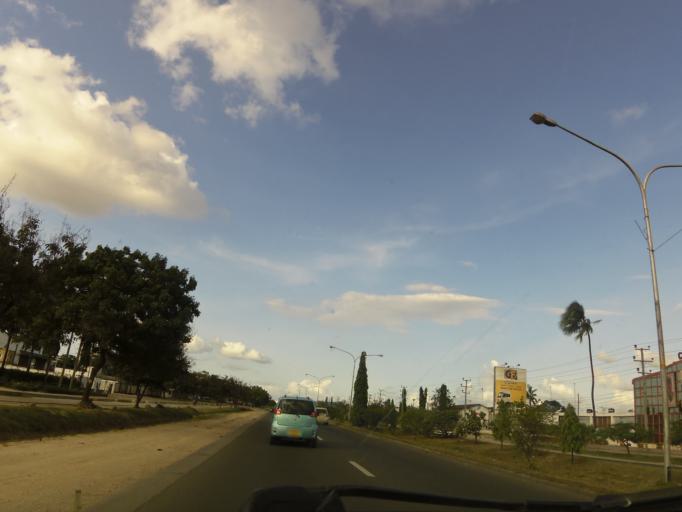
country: TZ
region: Dar es Salaam
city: Dar es Salaam
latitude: -6.8560
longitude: 39.2215
